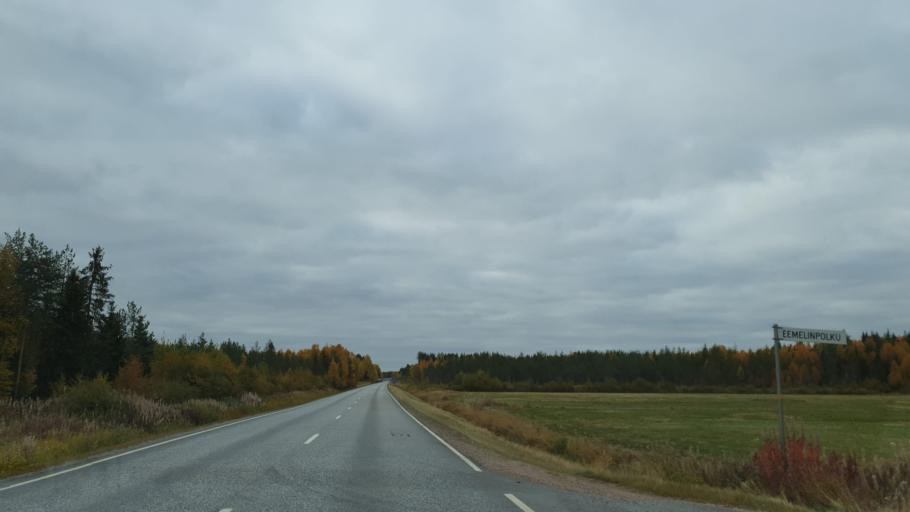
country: FI
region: Lapland
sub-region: Rovaniemi
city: Rovaniemi
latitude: 66.7988
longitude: 25.4144
